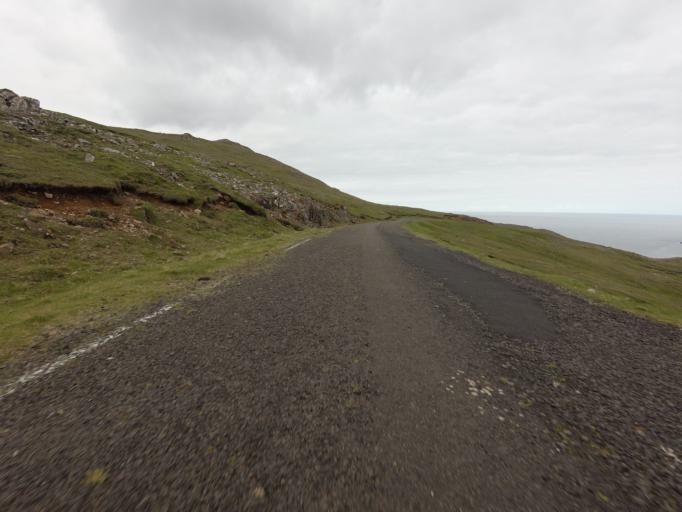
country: FO
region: Suduroy
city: Vagur
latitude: 61.4371
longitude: -6.7549
